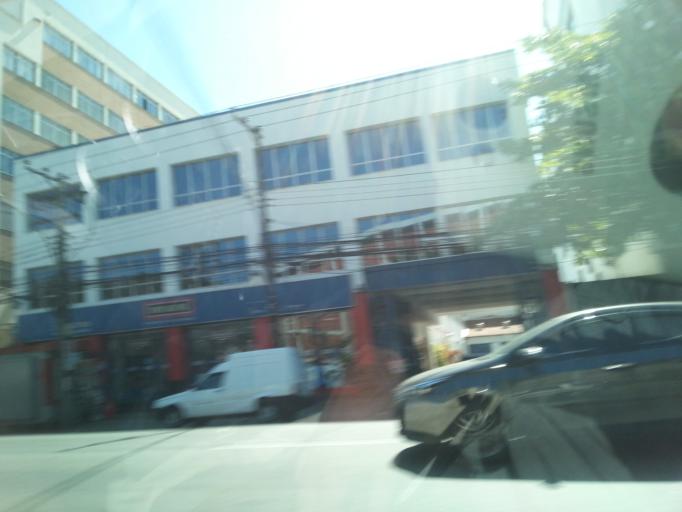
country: BR
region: Rio de Janeiro
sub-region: Rio De Janeiro
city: Rio de Janeiro
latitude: -22.8969
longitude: -43.2215
